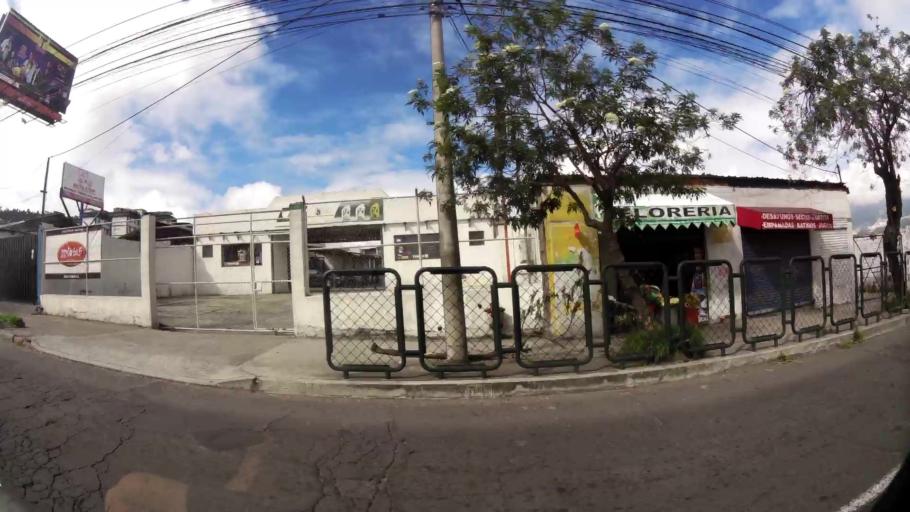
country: EC
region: Pichincha
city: Quito
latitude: -0.1643
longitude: -78.4709
